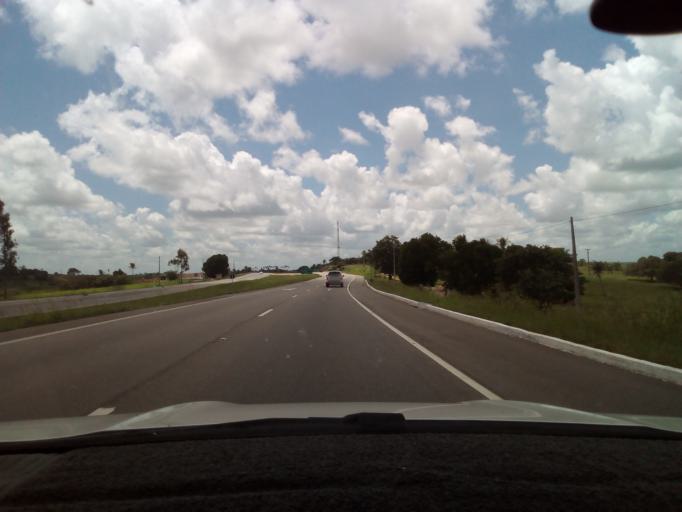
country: BR
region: Paraiba
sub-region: Pilar
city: Pilar
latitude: -7.1911
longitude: -35.2387
